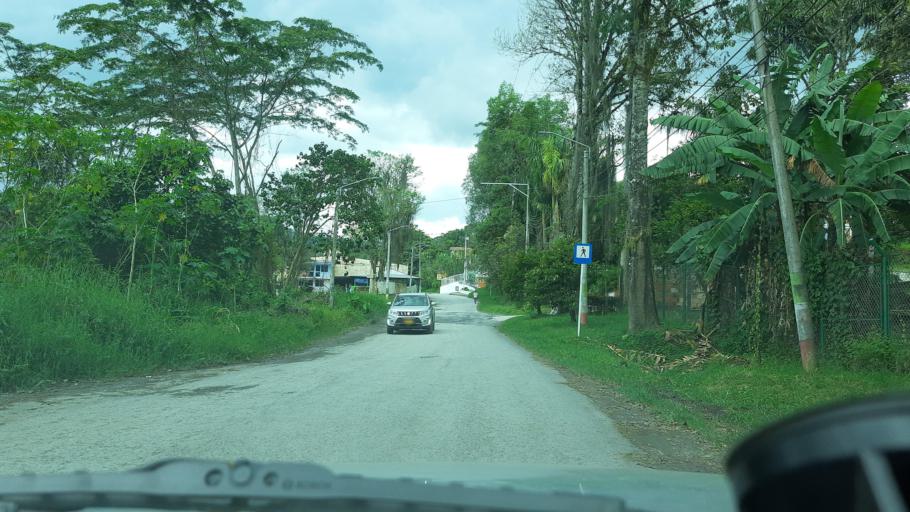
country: CO
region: Boyaca
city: Moniquira
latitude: 5.8828
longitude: -73.5775
